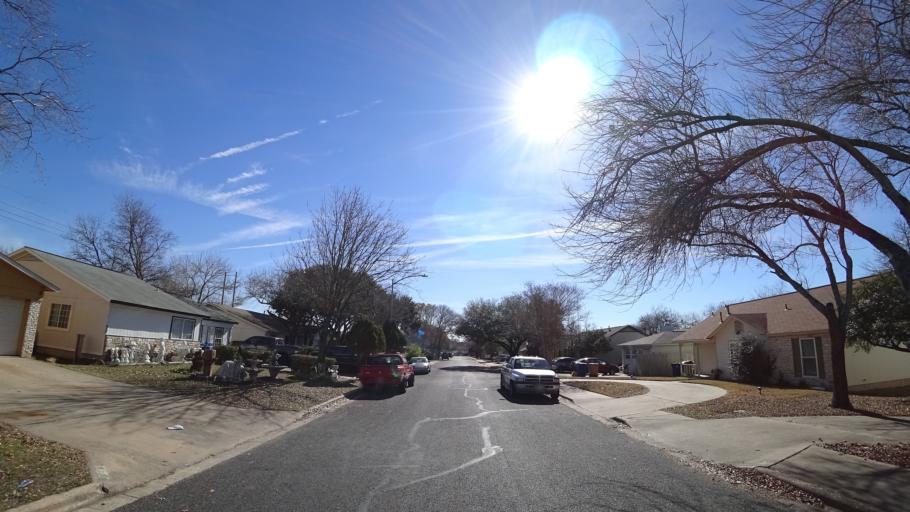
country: US
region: Texas
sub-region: Travis County
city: Wells Branch
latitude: 30.3696
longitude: -97.6895
